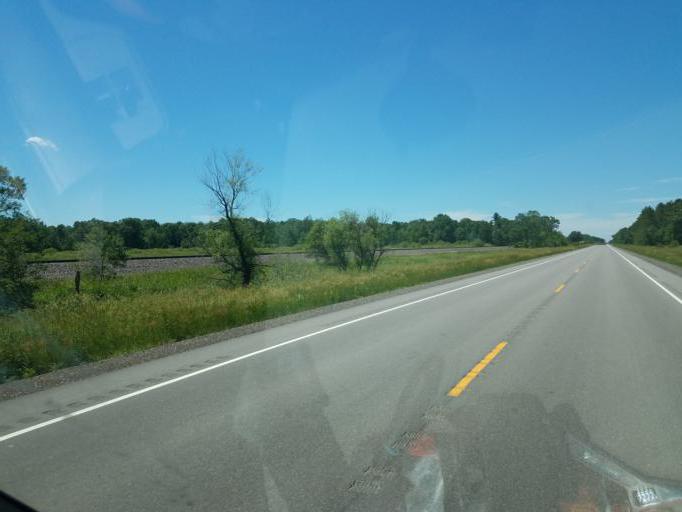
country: US
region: Wisconsin
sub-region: Juneau County
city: New Lisbon
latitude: 44.0251
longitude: -90.1726
